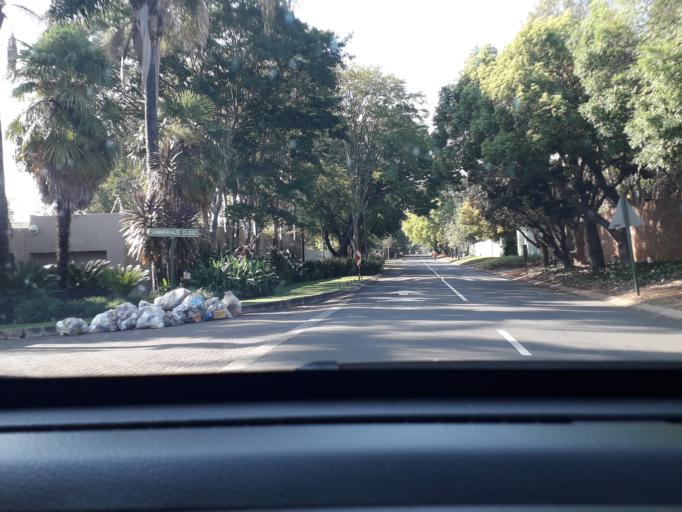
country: ZA
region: Gauteng
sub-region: City of Johannesburg Metropolitan Municipality
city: Modderfontein
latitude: -26.0770
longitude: 28.0495
